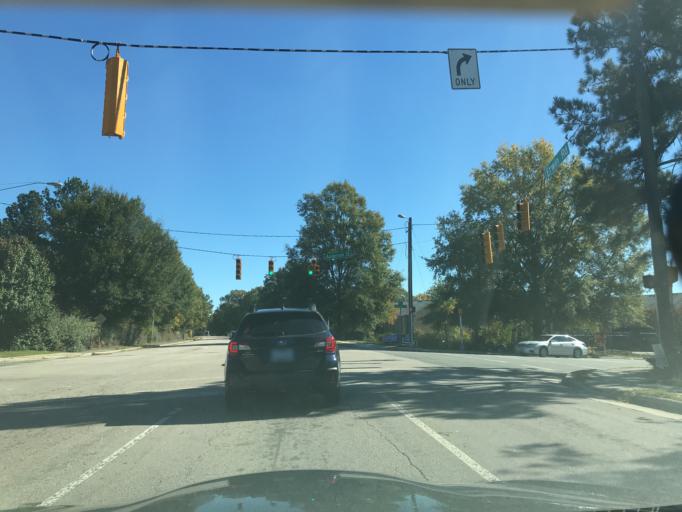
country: US
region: North Carolina
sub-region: Durham County
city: Durham
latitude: 36.0068
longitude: -78.9301
